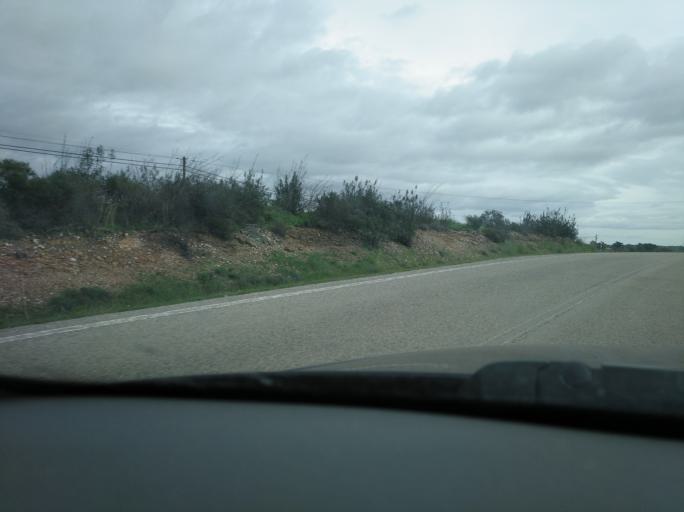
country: PT
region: Faro
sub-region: Castro Marim
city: Castro Marim
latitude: 37.2213
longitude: -7.4787
